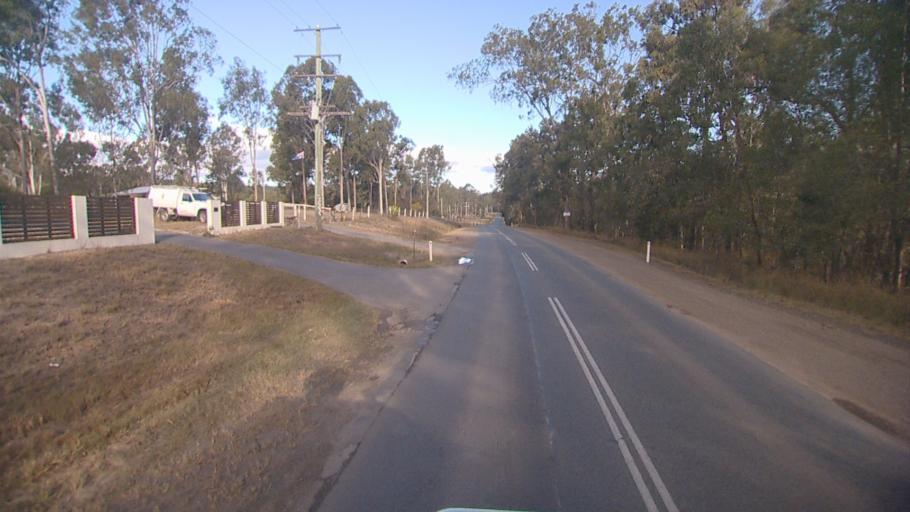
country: AU
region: Queensland
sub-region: Logan
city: Cedar Vale
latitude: -27.8565
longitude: 153.0536
